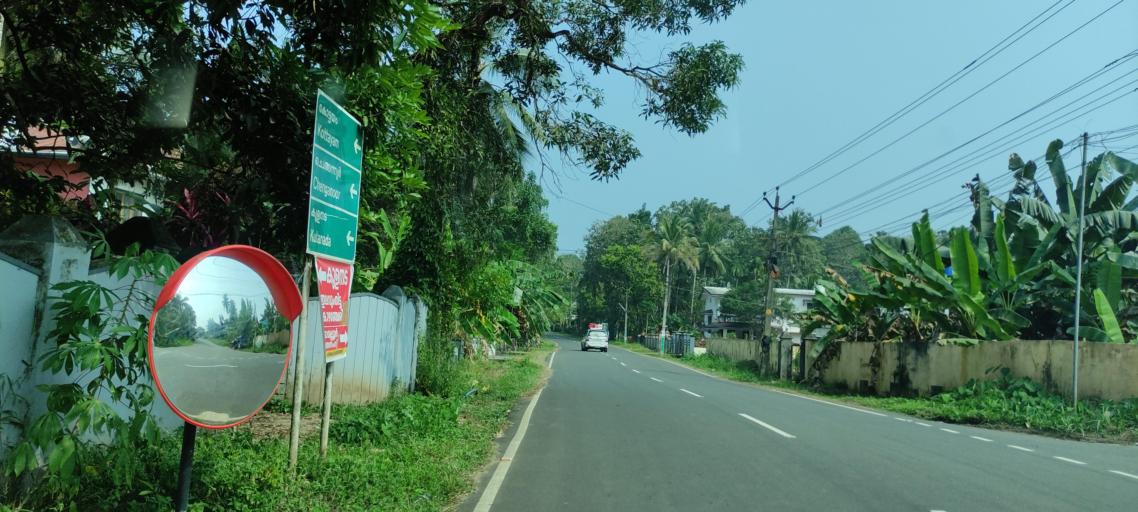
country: IN
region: Kerala
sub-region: Pattanamtitta
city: Adur
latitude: 9.2300
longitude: 76.7126
